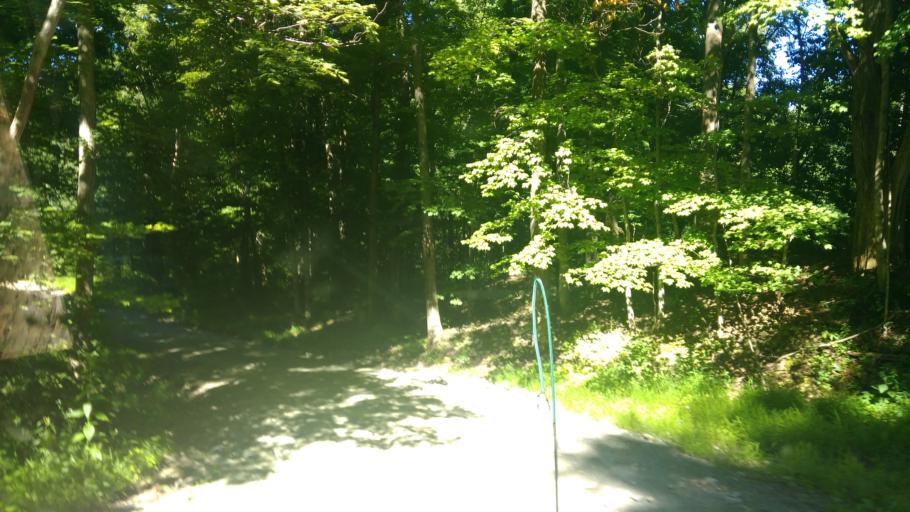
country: US
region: New York
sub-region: Wayne County
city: Clyde
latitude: 43.0245
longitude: -76.8715
